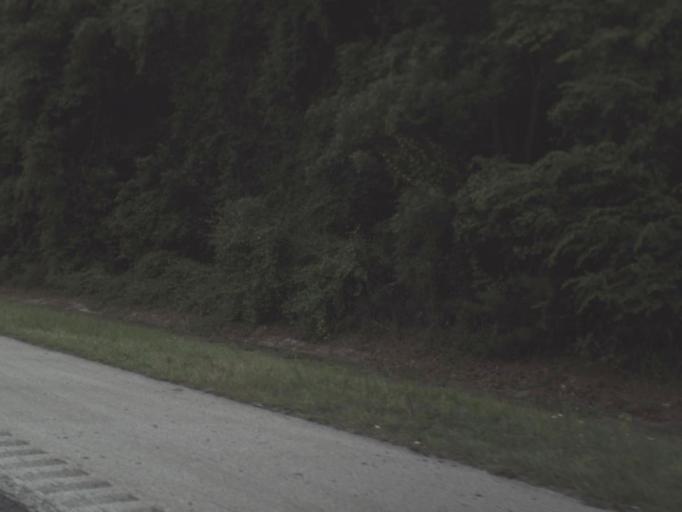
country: US
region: Florida
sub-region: Alachua County
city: Gainesville
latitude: 29.4838
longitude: -82.2871
